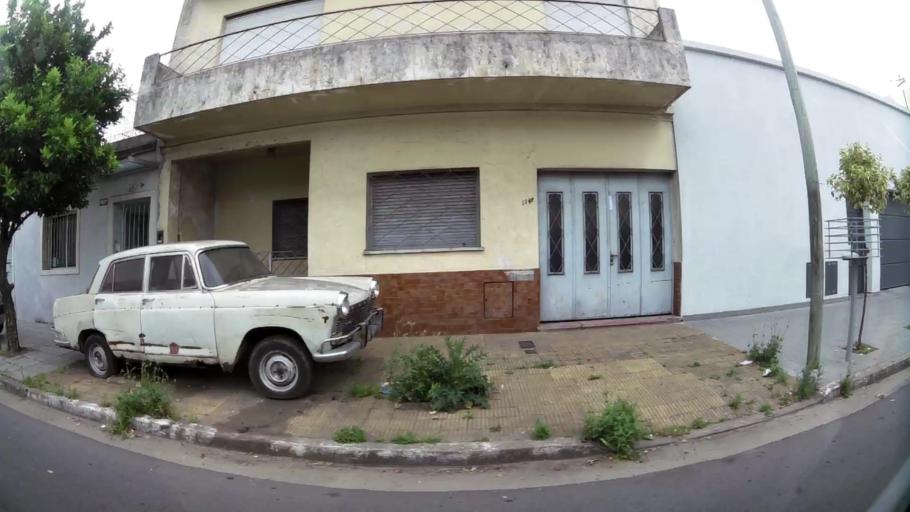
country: AR
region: Buenos Aires F.D.
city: Villa Lugano
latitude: -34.6714
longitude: -58.5121
